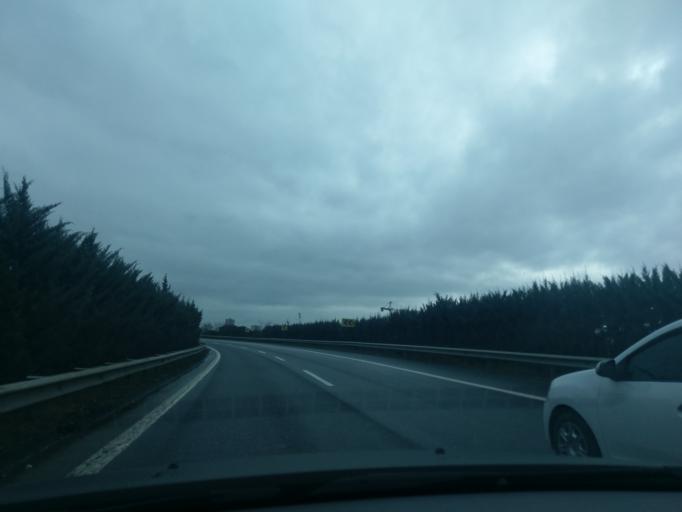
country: TR
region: Istanbul
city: Mahmutbey
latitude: 41.0616
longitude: 28.8403
